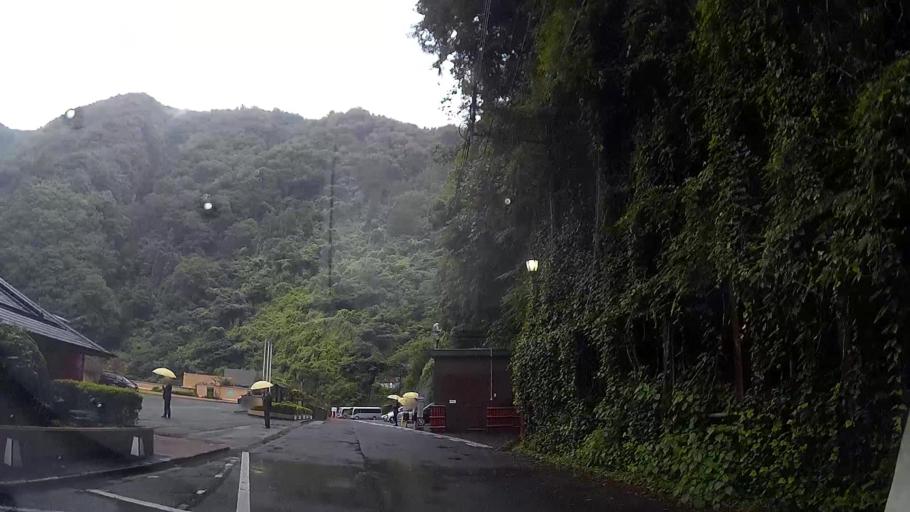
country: JP
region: Oita
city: Tsukawaki
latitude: 33.1862
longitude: 131.0311
